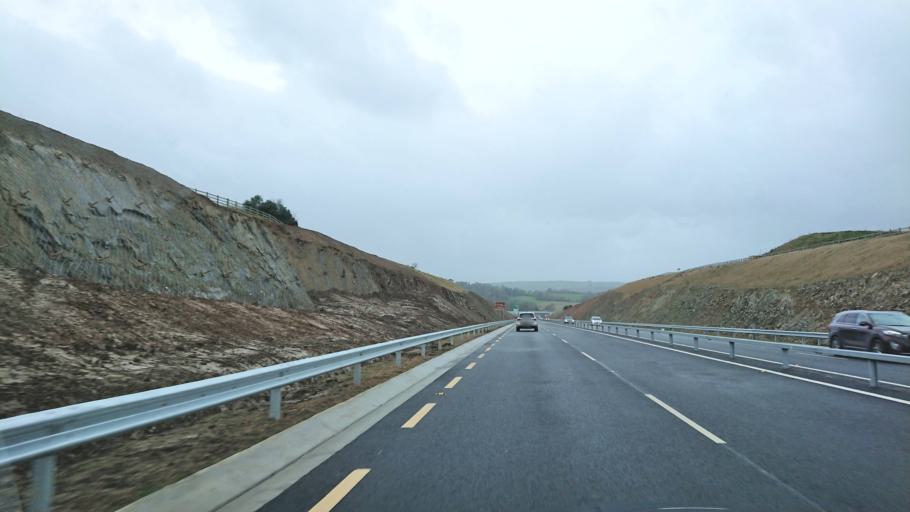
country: IE
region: Leinster
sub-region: Loch Garman
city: New Ross
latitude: 52.3677
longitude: -6.9457
